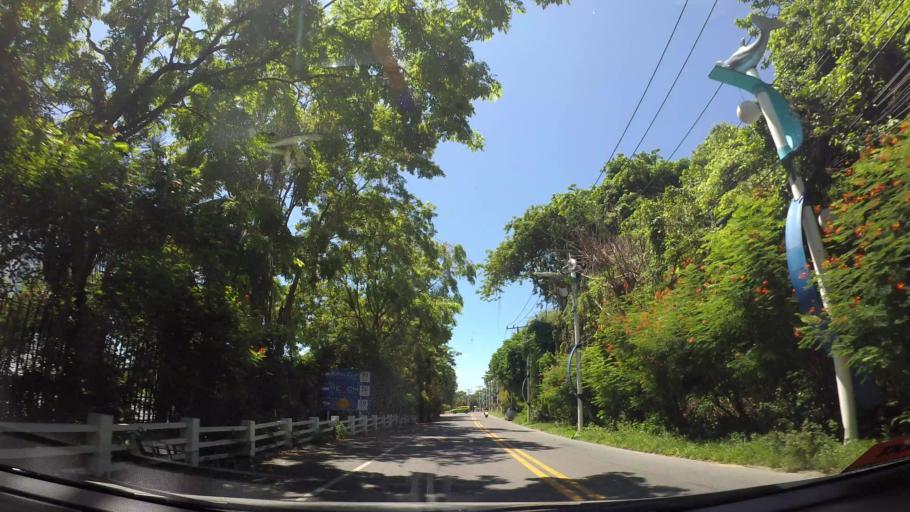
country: TH
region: Chon Buri
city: Phatthaya
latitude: 12.9222
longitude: 100.8651
